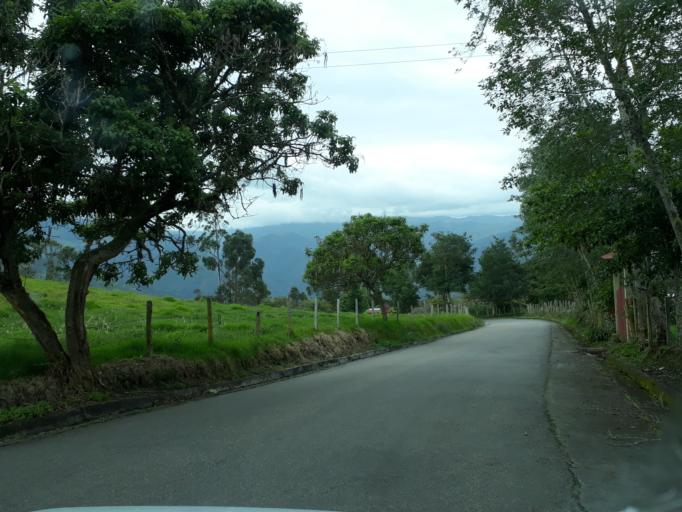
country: CO
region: Cundinamarca
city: Junin
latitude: 4.8010
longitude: -73.6777
